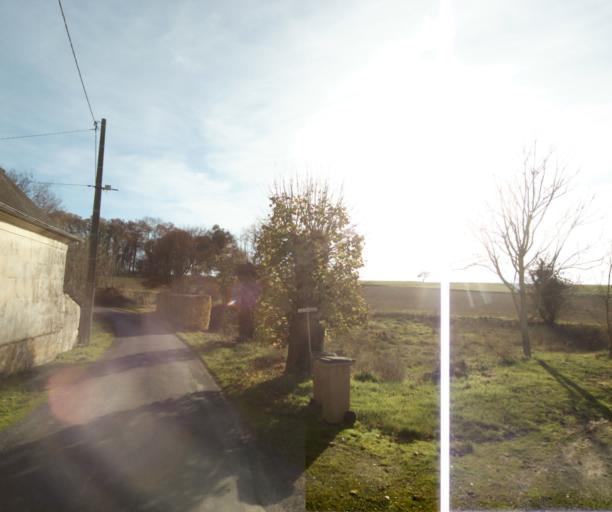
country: FR
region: Poitou-Charentes
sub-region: Departement de la Charente-Maritime
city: Chaniers
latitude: 45.7312
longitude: -0.5483
